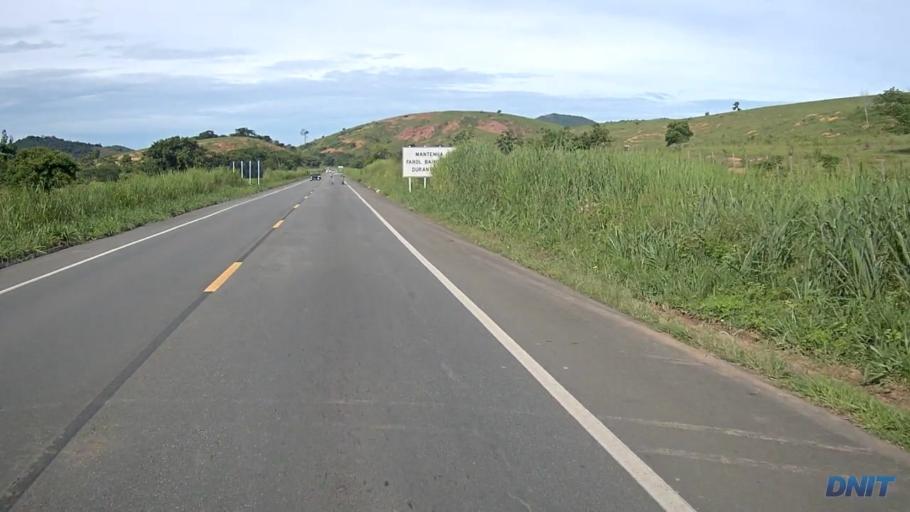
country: BR
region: Minas Gerais
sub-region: Belo Oriente
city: Belo Oriente
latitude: -19.2063
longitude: -42.2979
